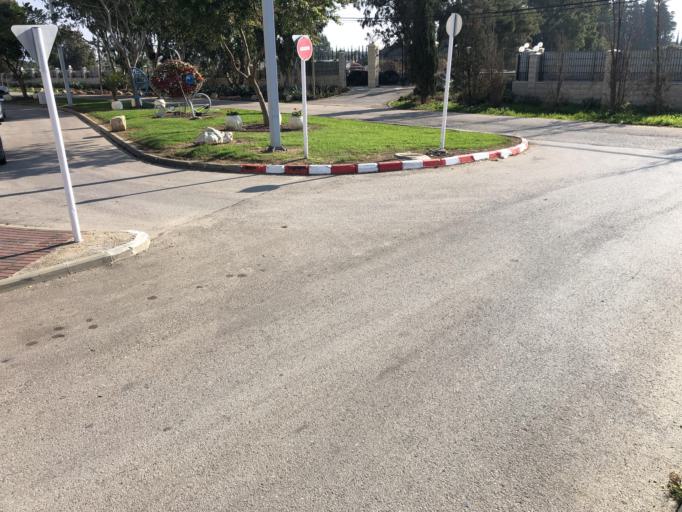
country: IL
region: Northern District
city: `Akko
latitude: 32.9179
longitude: 35.0909
